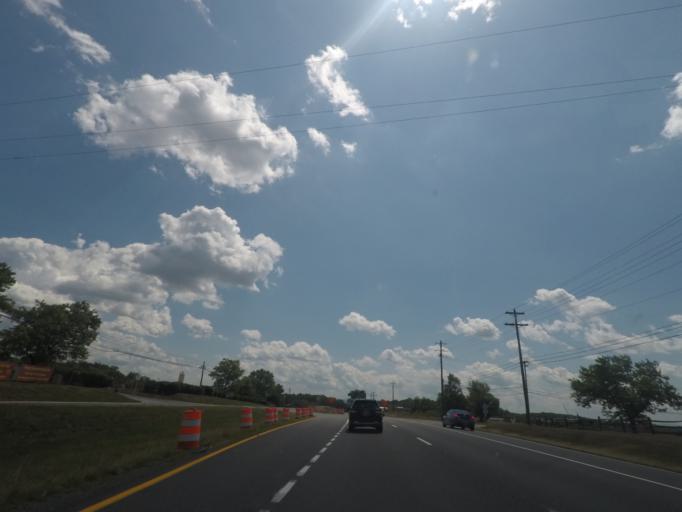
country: US
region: Virginia
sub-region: City of Winchester
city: Winchester
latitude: 39.1443
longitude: -78.1276
